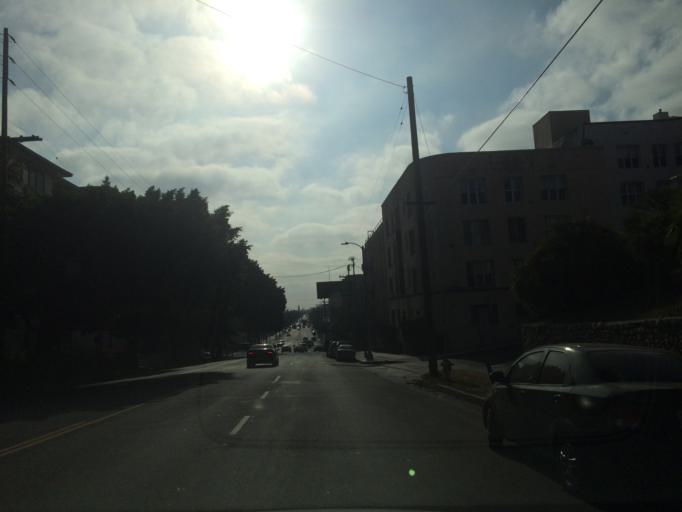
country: US
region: California
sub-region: Los Angeles County
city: View Park-Windsor Hills
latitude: 34.0327
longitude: -118.3105
